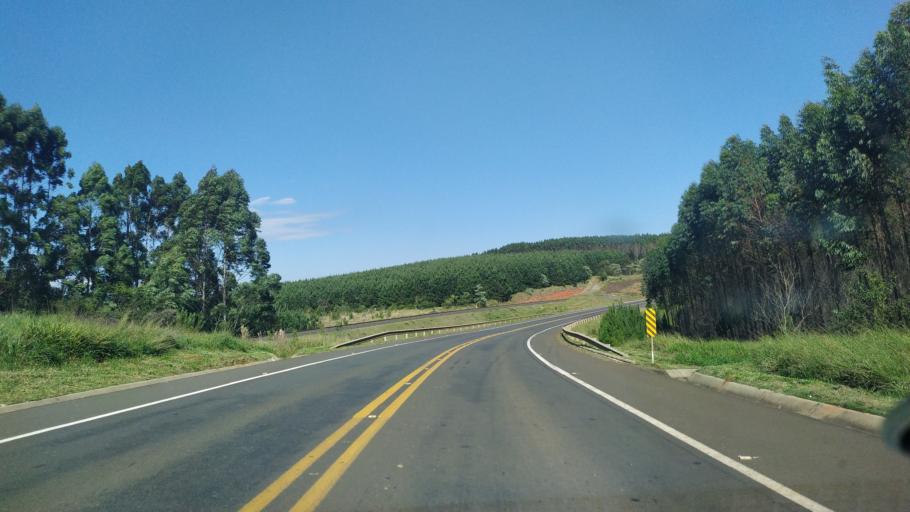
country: BR
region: Parana
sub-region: Telemaco Borba
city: Telemaco Borba
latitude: -24.2524
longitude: -50.7769
